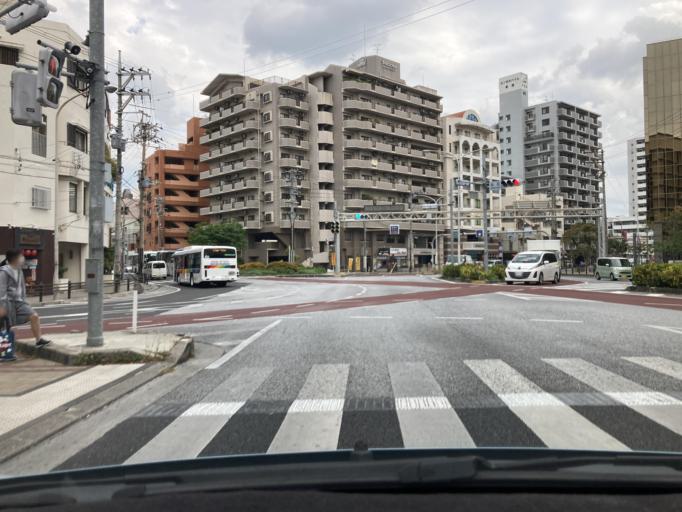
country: JP
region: Okinawa
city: Naha-shi
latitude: 26.2104
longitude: 127.6776
